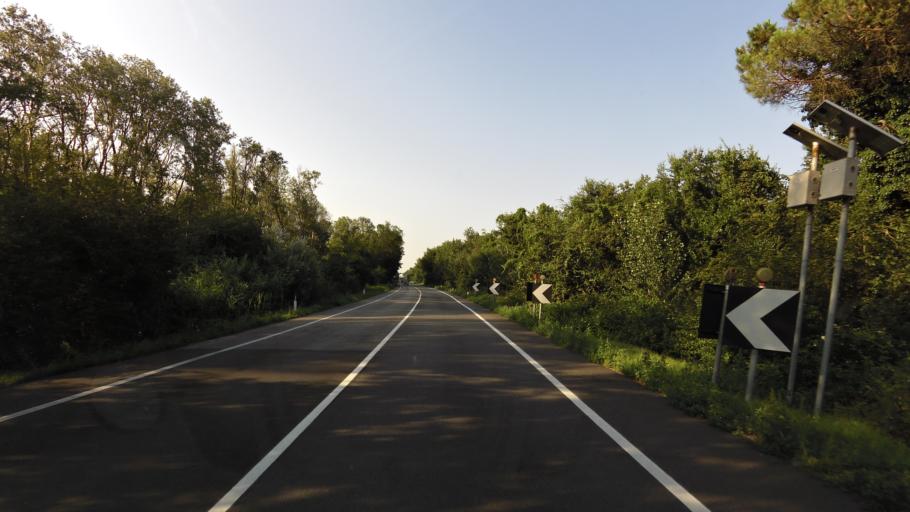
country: IT
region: Emilia-Romagna
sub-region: Provincia di Ravenna
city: Marina Romea
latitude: 44.5150
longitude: 12.2266
